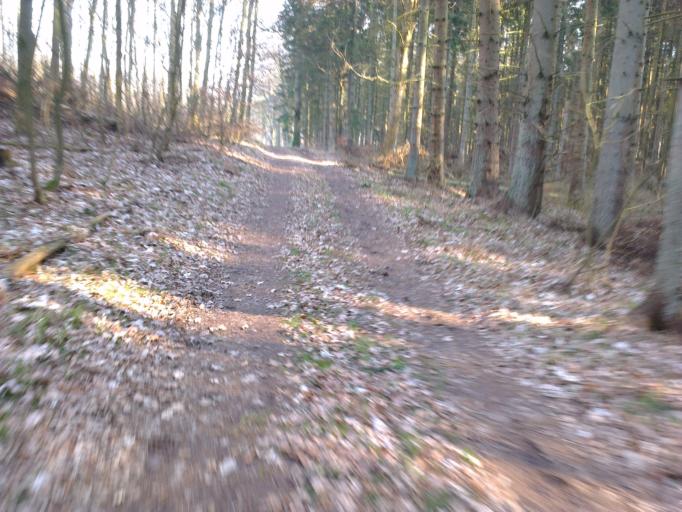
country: DK
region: Capital Region
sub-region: Frederikssund Kommune
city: Jaegerspris
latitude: 55.8801
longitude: 11.9938
